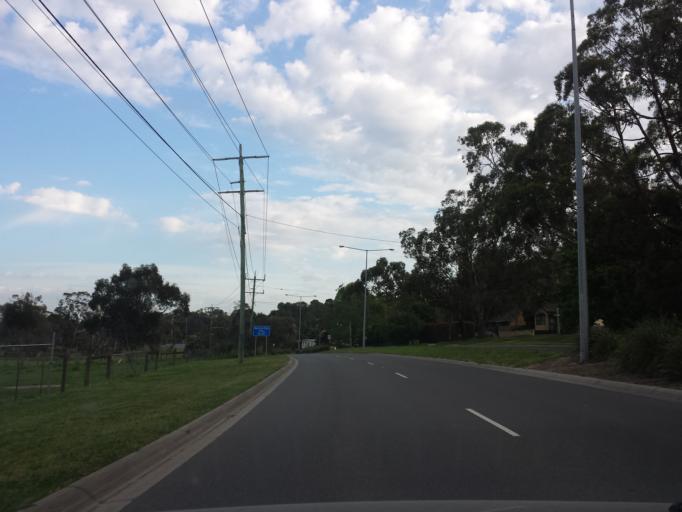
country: AU
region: Victoria
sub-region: Yarra Ranges
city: Mount Evelyn
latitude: -37.7721
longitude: 145.3628
